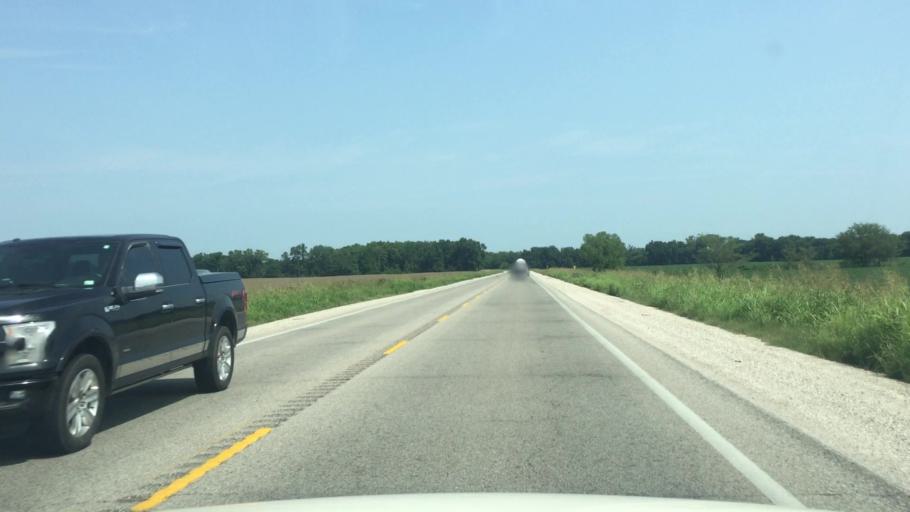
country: US
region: Kansas
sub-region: Montgomery County
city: Cherryvale
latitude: 37.1709
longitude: -95.5765
